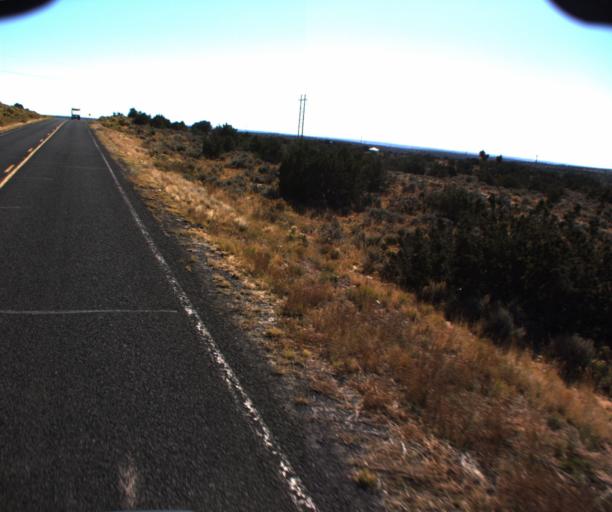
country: US
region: Arizona
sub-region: Apache County
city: Ganado
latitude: 35.6754
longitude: -109.5497
